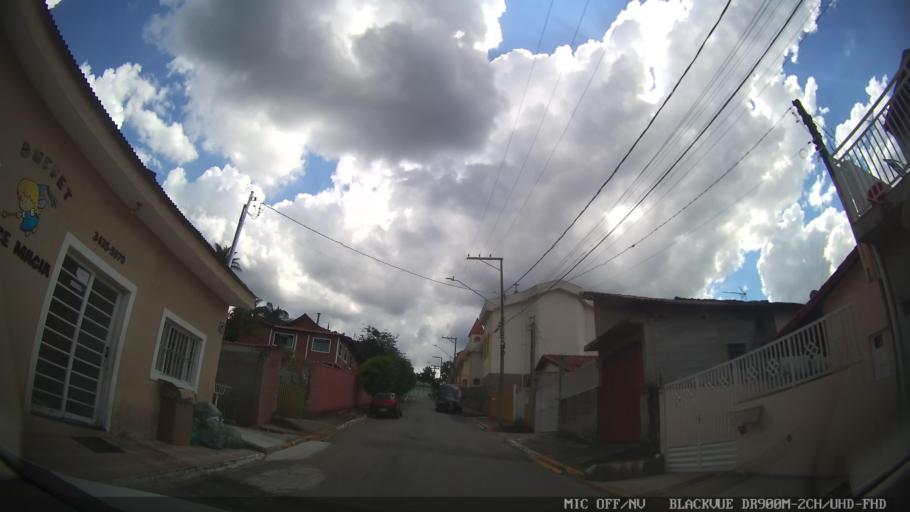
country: BR
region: Minas Gerais
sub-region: Extrema
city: Extrema
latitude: -22.8593
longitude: -46.3137
